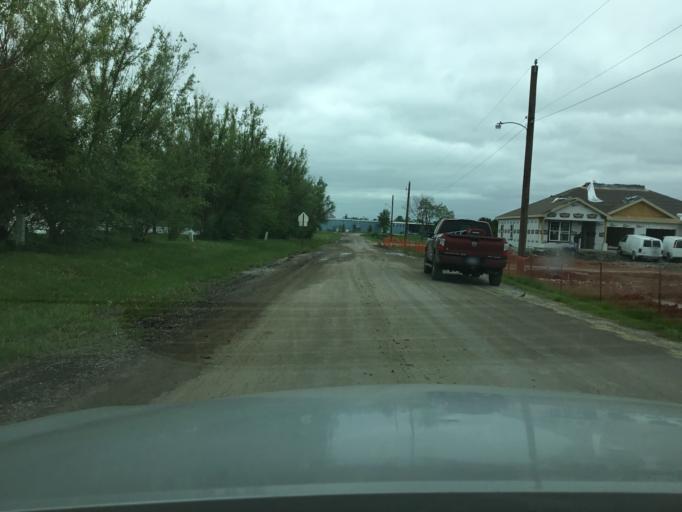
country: US
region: Kansas
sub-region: Franklin County
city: Ottawa
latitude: 38.6351
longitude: -95.2586
